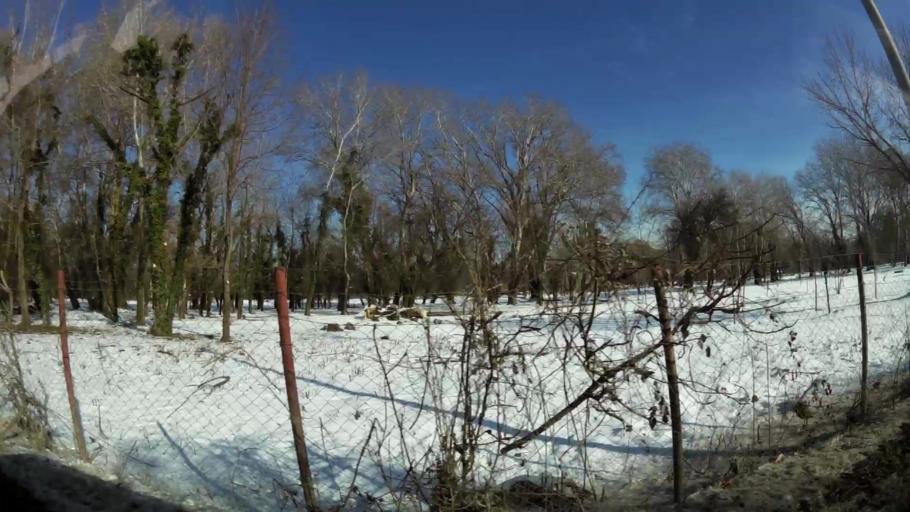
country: MK
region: Saraj
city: Saraj
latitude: 42.0000
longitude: 21.3390
